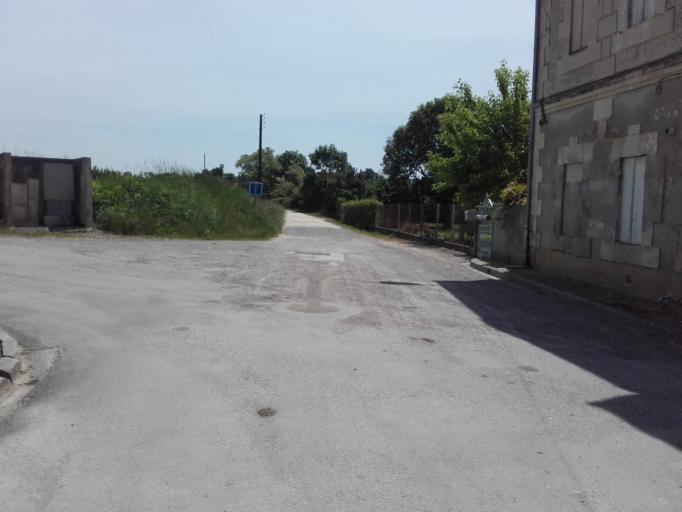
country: FR
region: Aquitaine
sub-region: Departement de la Gironde
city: Saint-Estephe
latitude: 45.2375
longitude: -0.7699
